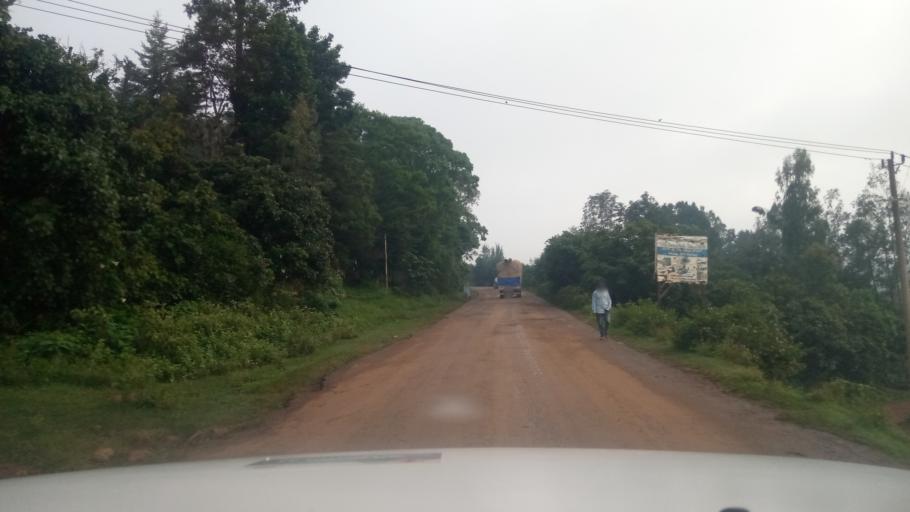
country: ET
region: Oromiya
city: Jima
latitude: 7.6896
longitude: 36.8259
